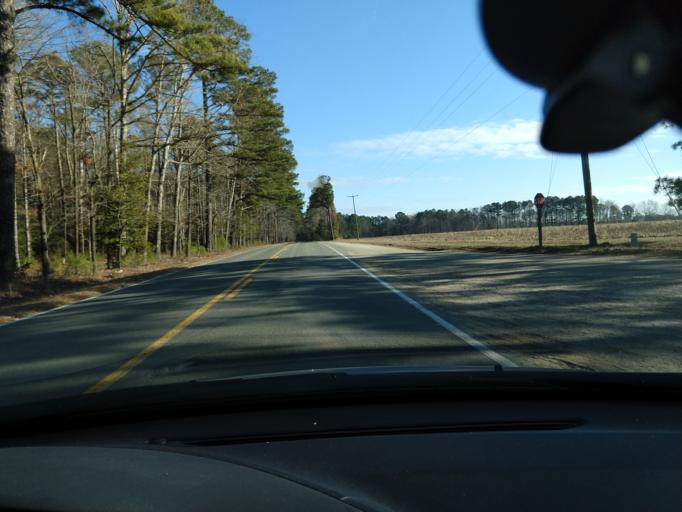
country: US
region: Virginia
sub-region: Surry County
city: Surry
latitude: 37.2664
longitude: -76.8956
